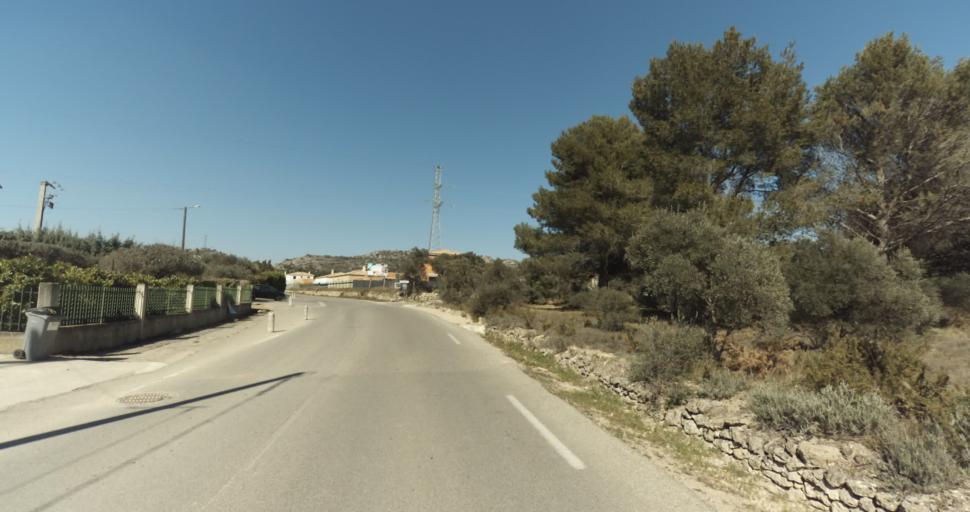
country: FR
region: Provence-Alpes-Cote d'Azur
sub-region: Departement des Bouches-du-Rhone
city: Pelissanne
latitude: 43.6409
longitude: 5.1544
